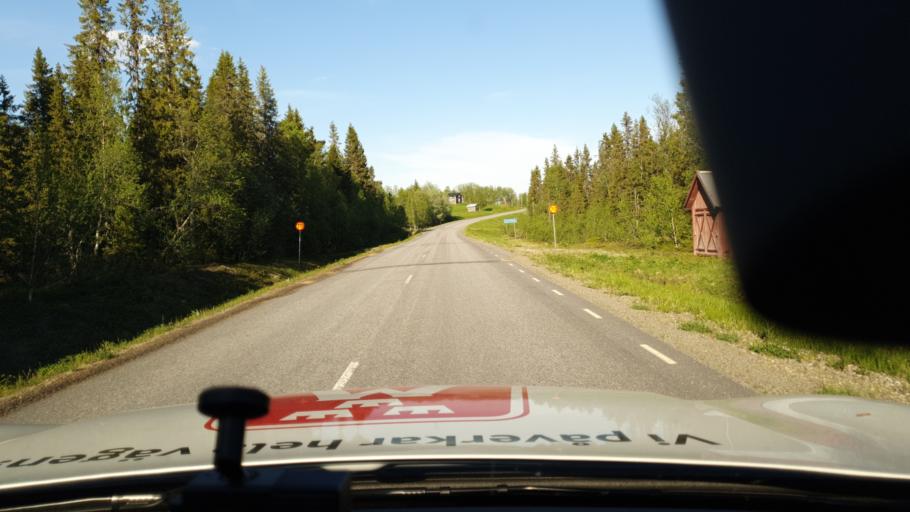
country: SE
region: Vaesterbotten
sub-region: Asele Kommun
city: Insjon
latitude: 64.7324
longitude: 17.3838
